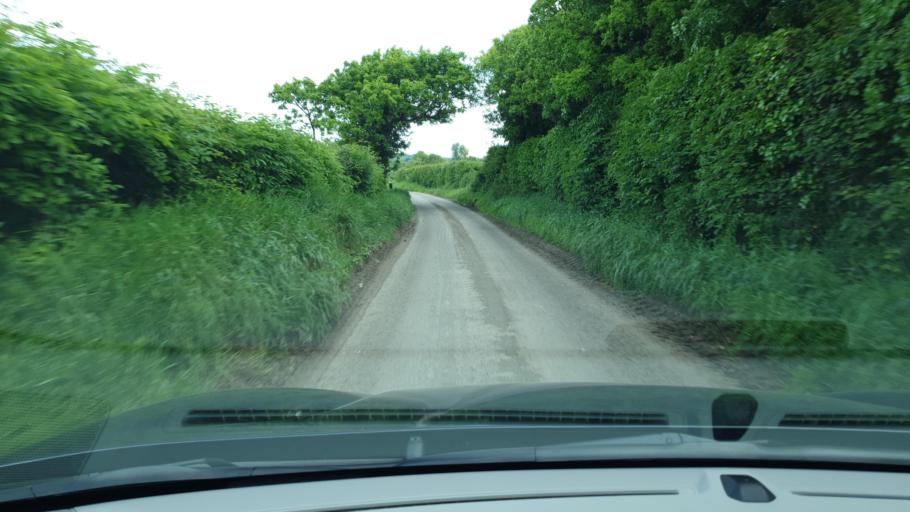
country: IE
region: Leinster
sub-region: An Mhi
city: Ratoath
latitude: 53.5665
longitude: -6.4503
